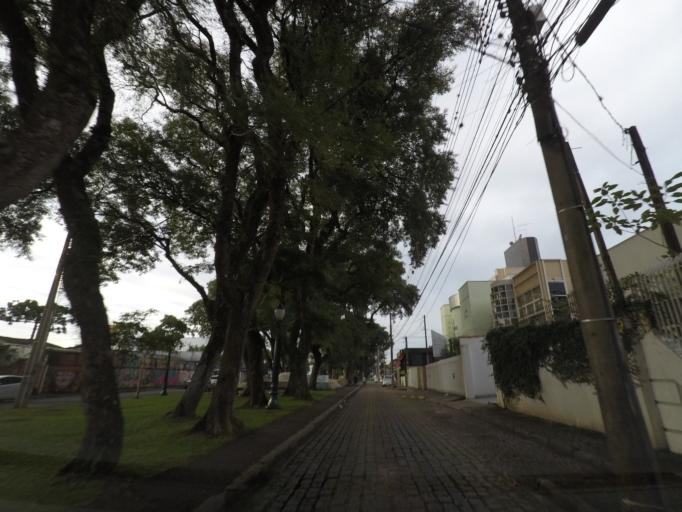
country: BR
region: Parana
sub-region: Curitiba
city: Curitiba
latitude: -25.4235
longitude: -49.2497
